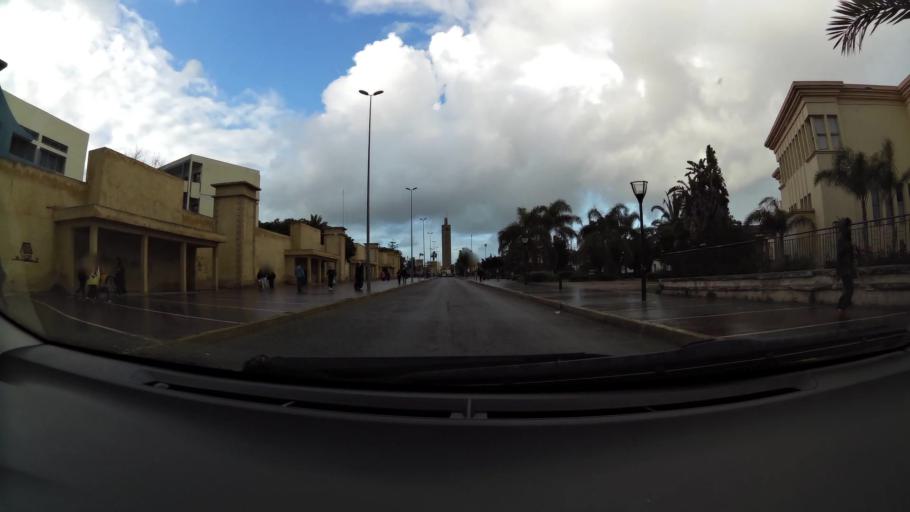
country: MA
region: Grand Casablanca
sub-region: Mohammedia
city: Mohammedia
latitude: 33.6846
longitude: -7.3904
